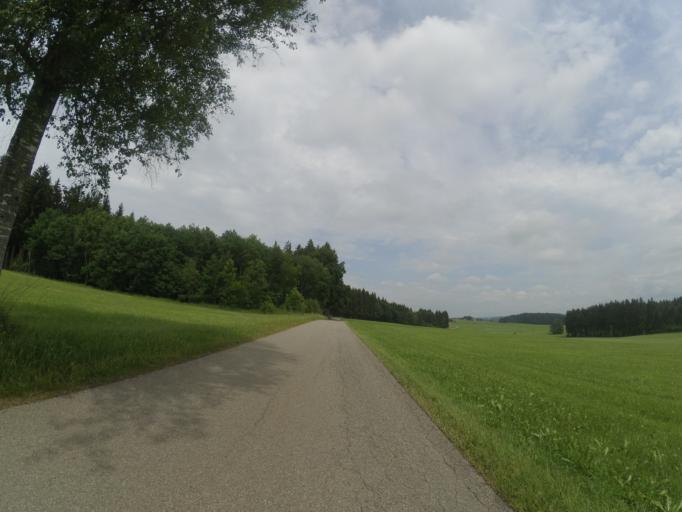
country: DE
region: Baden-Wuerttemberg
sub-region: Tuebingen Region
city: Leutkirch im Allgau
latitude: 47.7612
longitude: 10.0026
